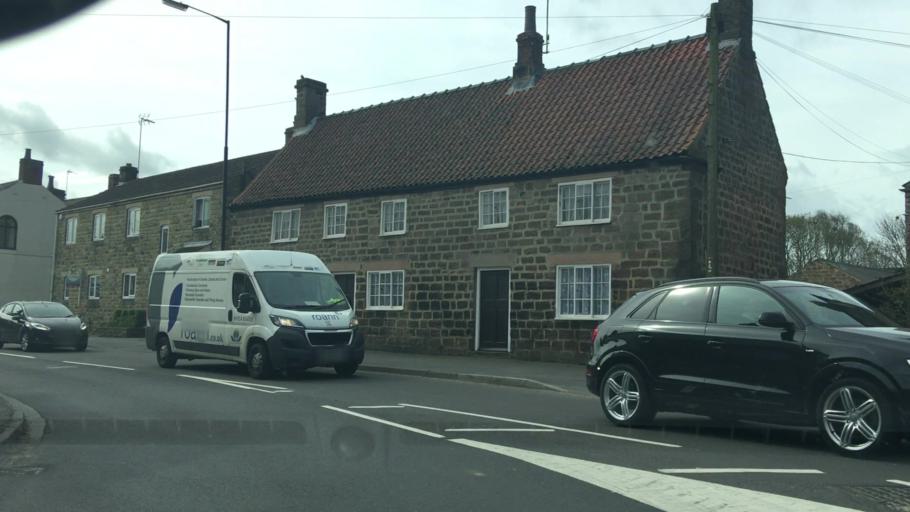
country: GB
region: England
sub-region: City and Borough of Leeds
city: Collingham
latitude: 53.9537
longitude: -1.4476
